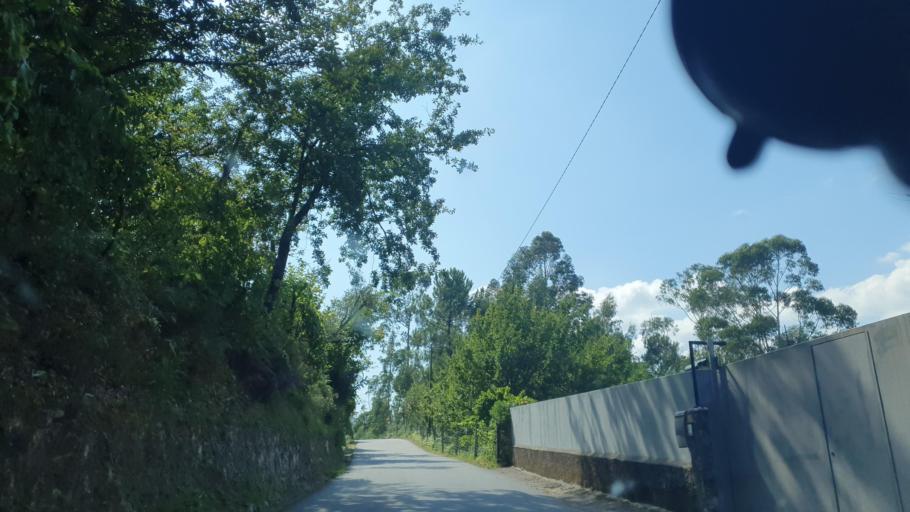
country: PT
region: Braga
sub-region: Vieira do Minho
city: Real
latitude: 41.6732
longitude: -8.1656
